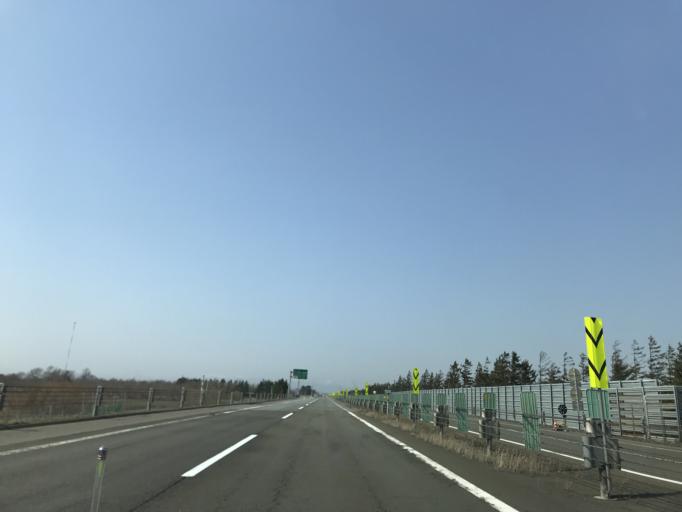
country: JP
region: Hokkaido
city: Ebetsu
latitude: 43.1081
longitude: 141.6065
